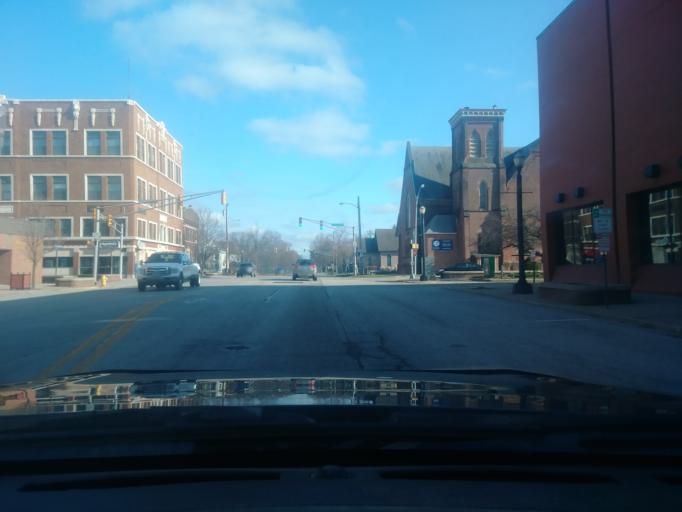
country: US
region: Indiana
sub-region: LaPorte County
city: LaPorte
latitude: 41.6103
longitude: -86.7221
